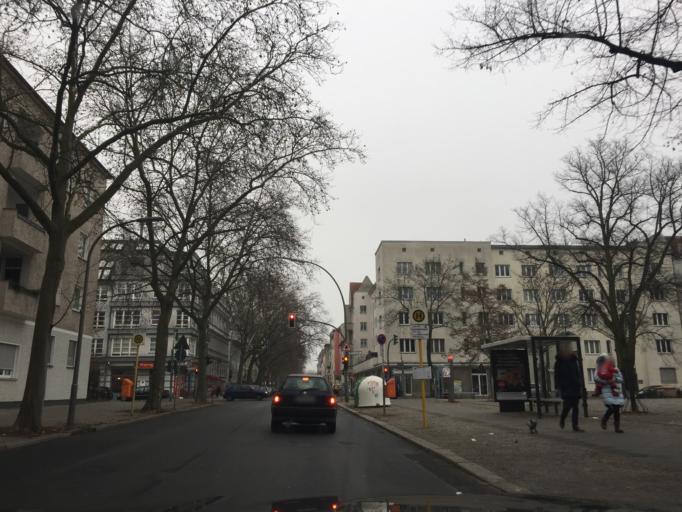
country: DE
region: Berlin
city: Wilhelmstadt
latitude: 52.5210
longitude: 13.1931
